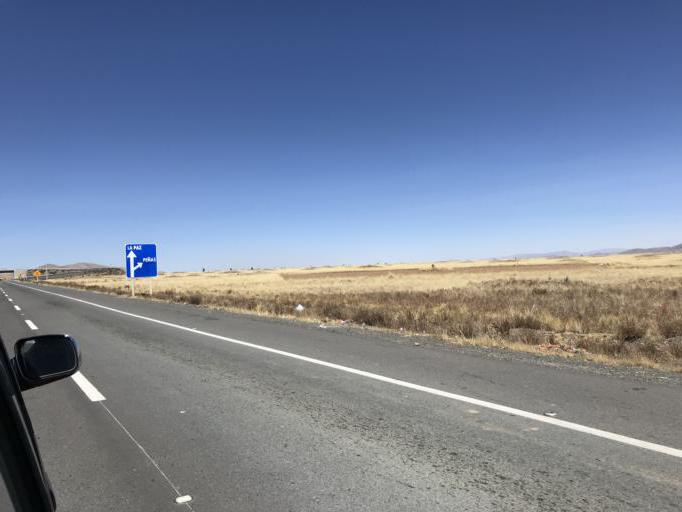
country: BO
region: La Paz
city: Batallas
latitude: -16.3173
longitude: -68.4423
